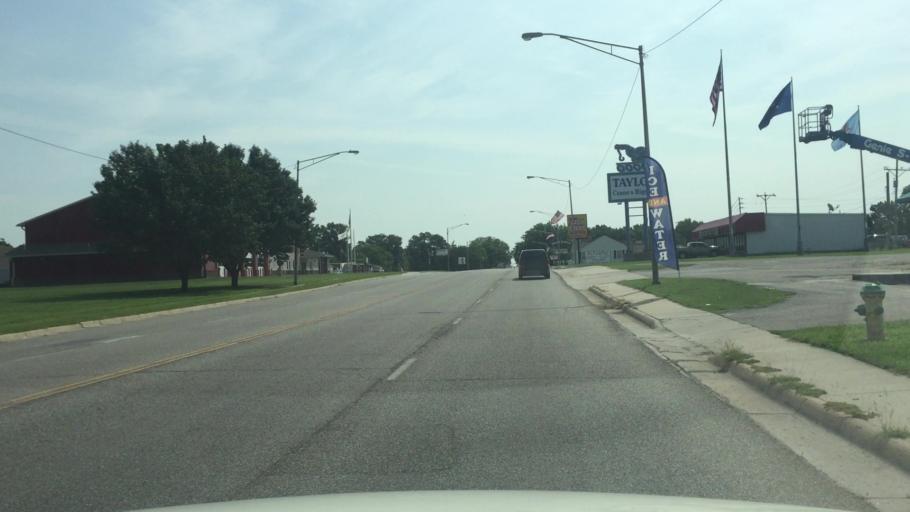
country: US
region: Kansas
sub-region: Montgomery County
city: Coffeyville
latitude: 37.0331
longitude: -95.6365
